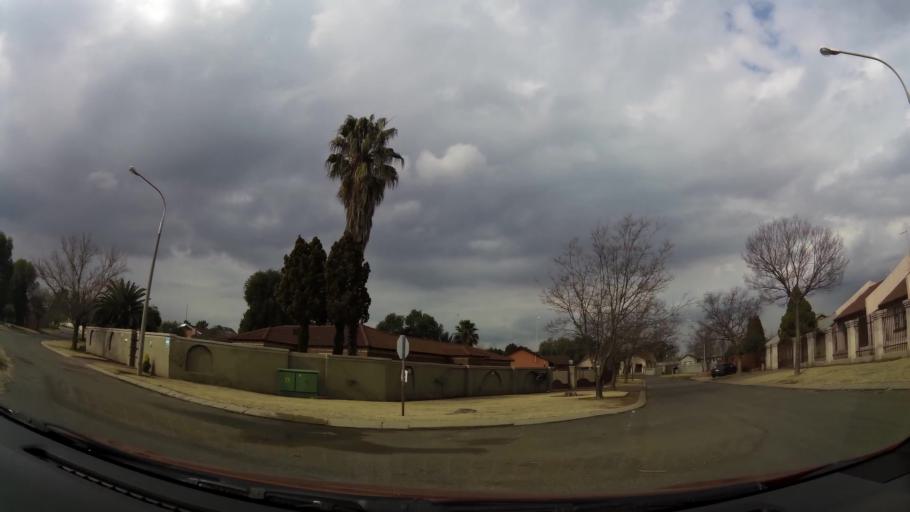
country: ZA
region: Gauteng
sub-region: Sedibeng District Municipality
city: Vanderbijlpark
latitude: -26.7089
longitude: 27.8019
